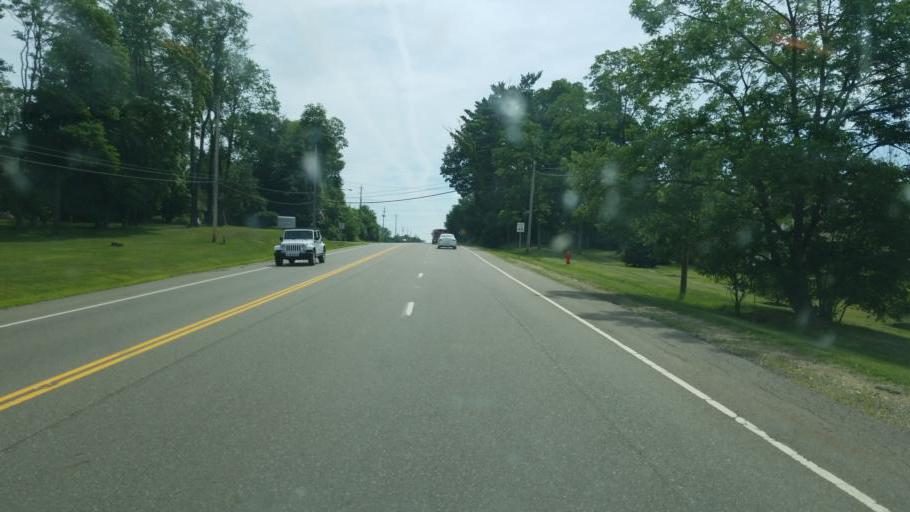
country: US
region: Ohio
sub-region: Summit County
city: Northfield
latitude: 41.3144
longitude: -81.5694
